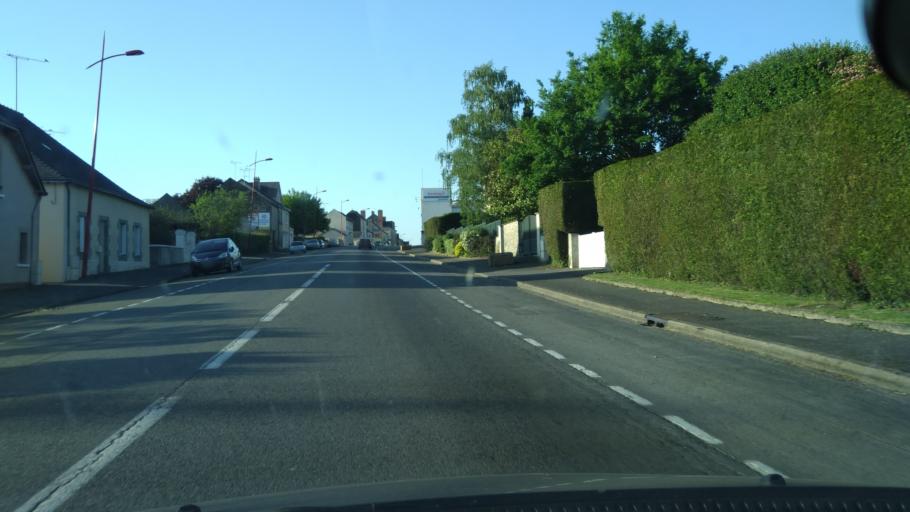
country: FR
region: Pays de la Loire
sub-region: Departement de la Mayenne
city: Cosse-le-Vivien
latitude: 47.9414
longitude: -0.9144
